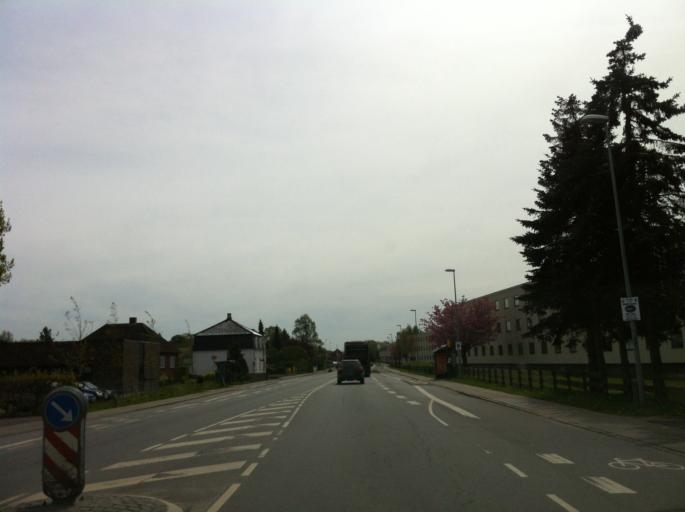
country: DK
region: Zealand
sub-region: Naestved Kommune
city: Naestved
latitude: 55.2526
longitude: 11.7579
